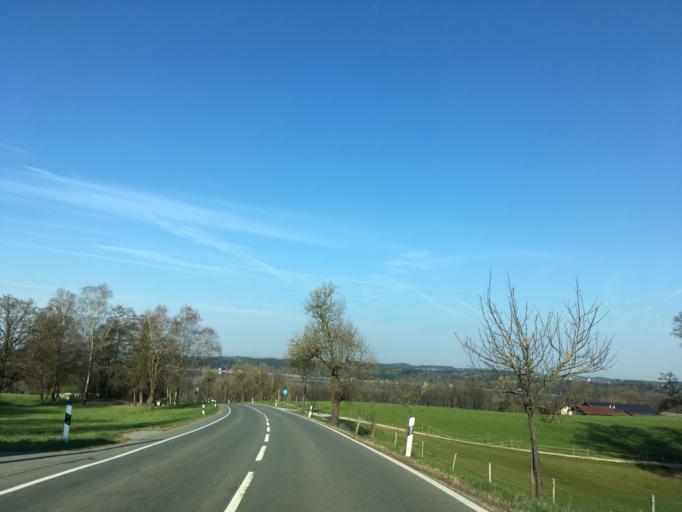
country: DE
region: Bavaria
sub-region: Upper Bavaria
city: Riedering
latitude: 47.8640
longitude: 12.2510
